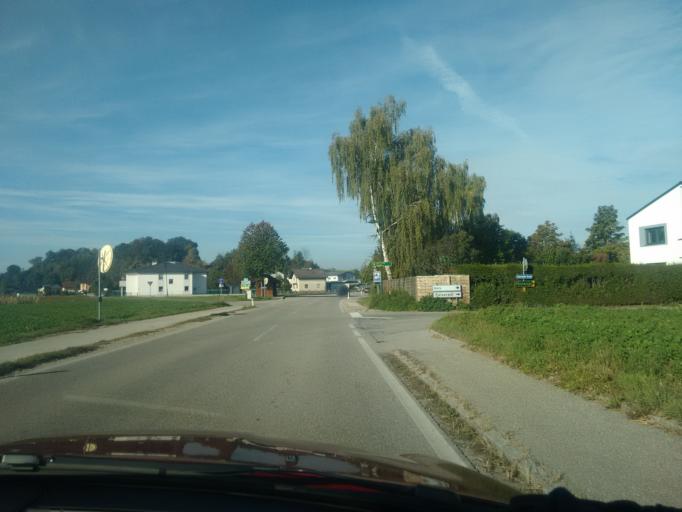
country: AT
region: Upper Austria
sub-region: Politischer Bezirk Vocklabruck
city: Oberndorf bei Schwanenstadt
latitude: 48.0542
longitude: 13.7548
